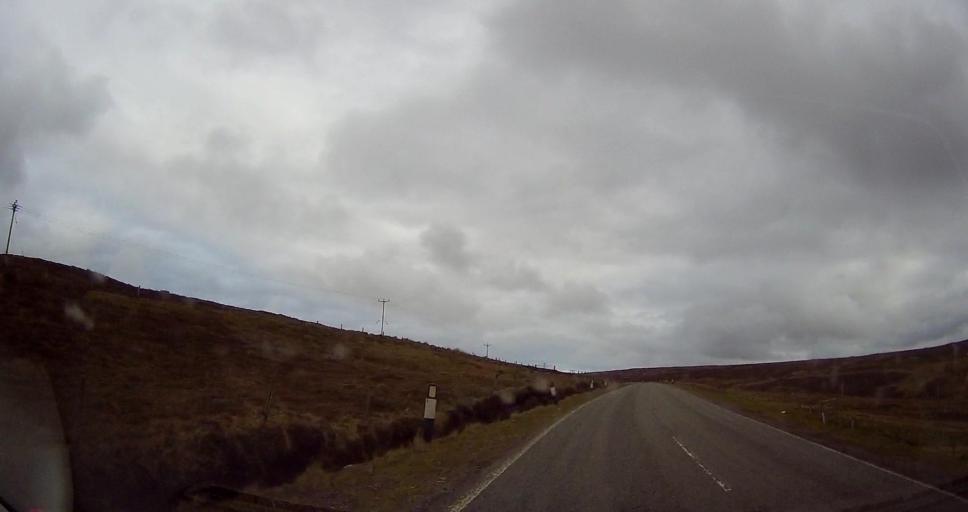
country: GB
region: Scotland
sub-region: Shetland Islands
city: Shetland
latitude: 60.6140
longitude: -1.0746
